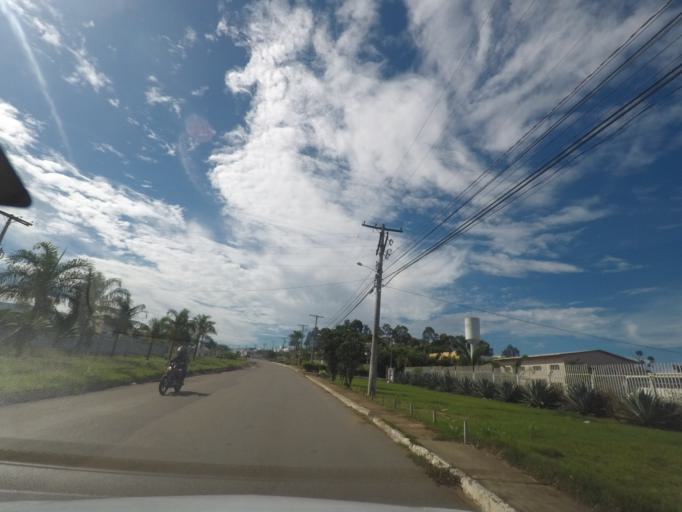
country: BR
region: Goias
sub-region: Aparecida De Goiania
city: Aparecida de Goiania
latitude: -16.7938
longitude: -49.2619
